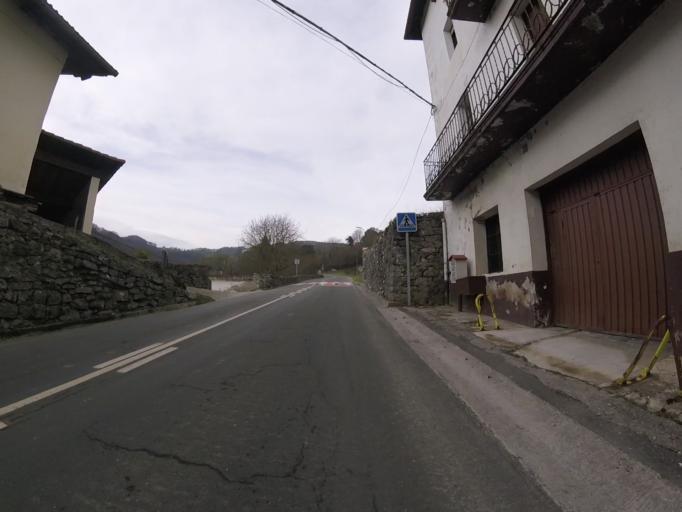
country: ES
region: Basque Country
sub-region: Provincia de Guipuzcoa
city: Errezil
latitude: 43.1424
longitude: -2.1683
